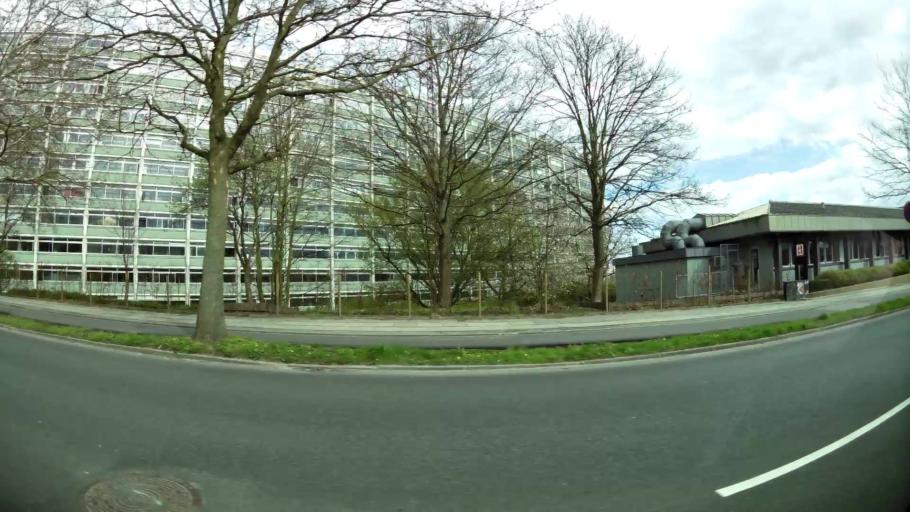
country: DK
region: Central Jutland
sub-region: Arhus Kommune
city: Arhus
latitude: 56.1620
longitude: 10.1967
